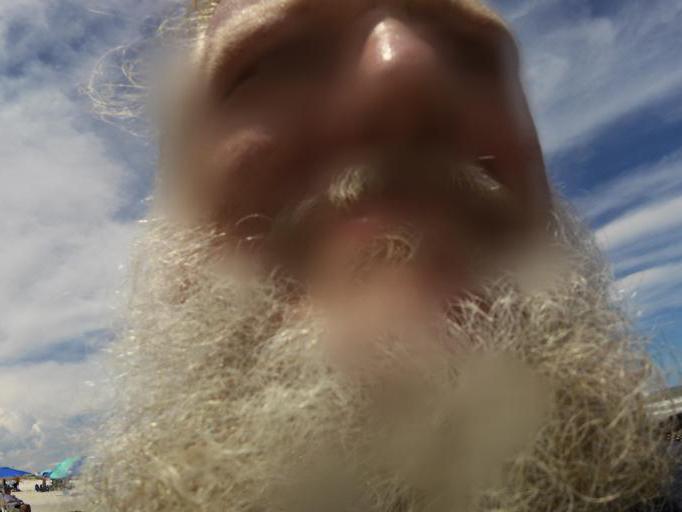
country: US
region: Florida
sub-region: Saint Johns County
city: Butler Beach
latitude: 29.8224
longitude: -81.2621
